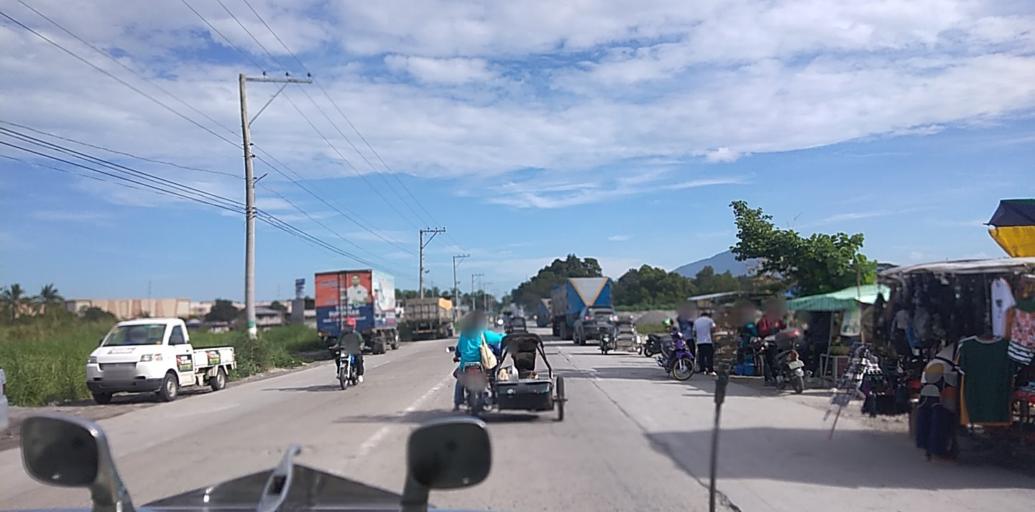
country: PH
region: Central Luzon
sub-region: Province of Pampanga
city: Bulaon
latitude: 15.1039
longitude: 120.6594
